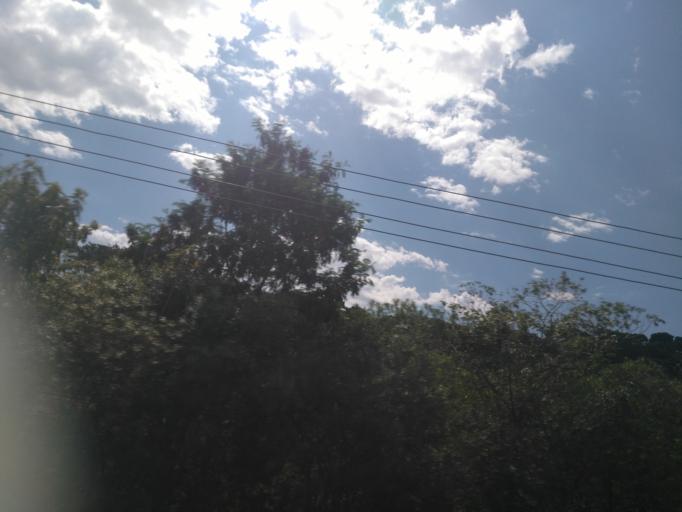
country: TZ
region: Mwanza
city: Mwanza
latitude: -2.5051
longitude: 32.9112
